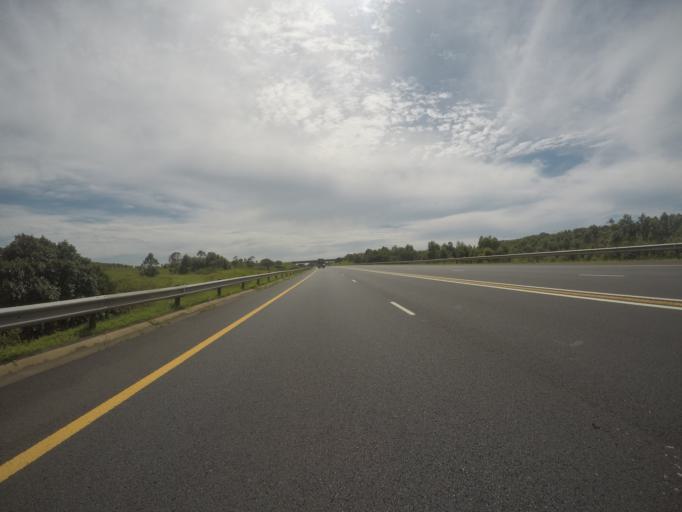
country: ZA
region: KwaZulu-Natal
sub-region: iLembe District Municipality
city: Mandeni
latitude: -29.1642
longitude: 31.5304
